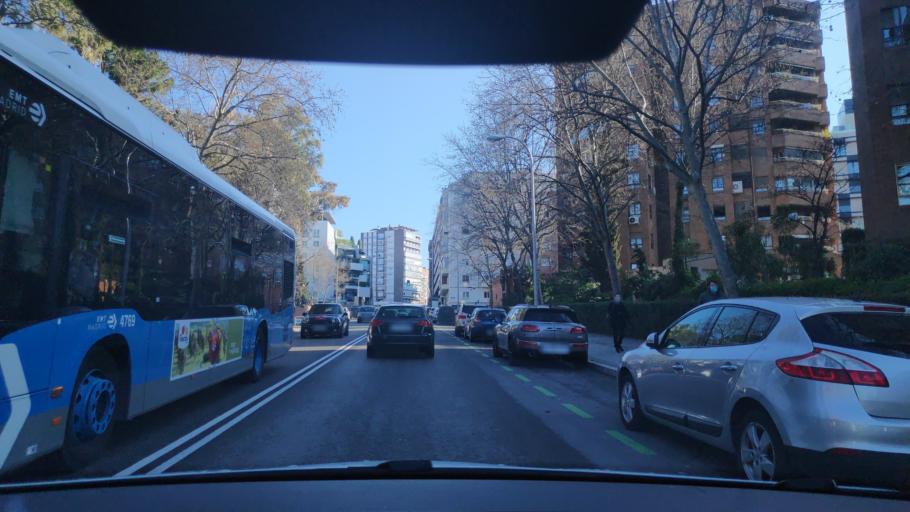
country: ES
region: Madrid
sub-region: Provincia de Madrid
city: Chamartin
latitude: 40.4547
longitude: -3.6831
